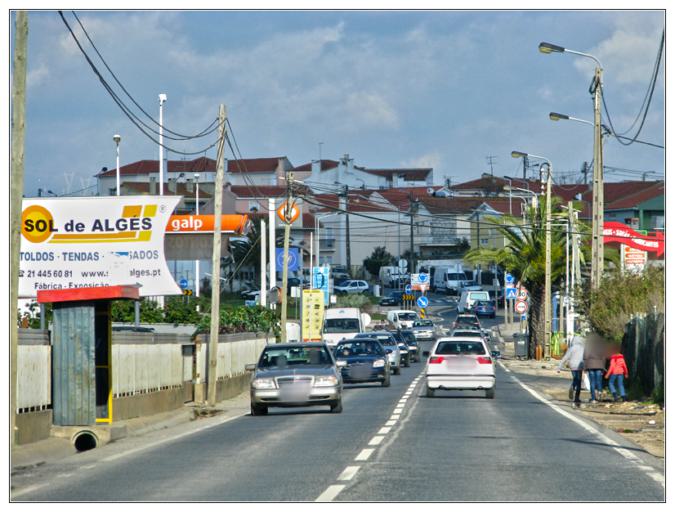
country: PT
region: Lisbon
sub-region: Cascais
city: Sao Domingos de Rana
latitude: 38.7227
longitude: -9.3369
